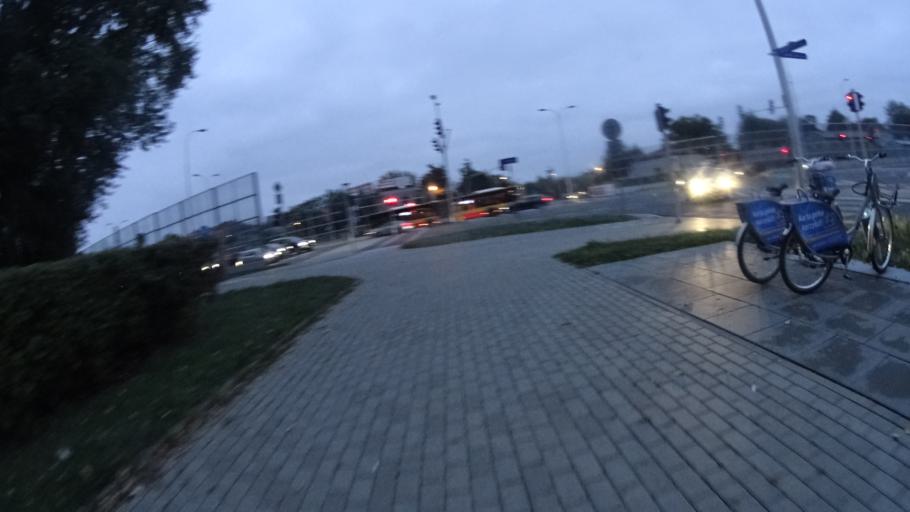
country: PL
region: Masovian Voivodeship
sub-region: Warszawa
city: Ursus
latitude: 52.2207
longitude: 20.8979
